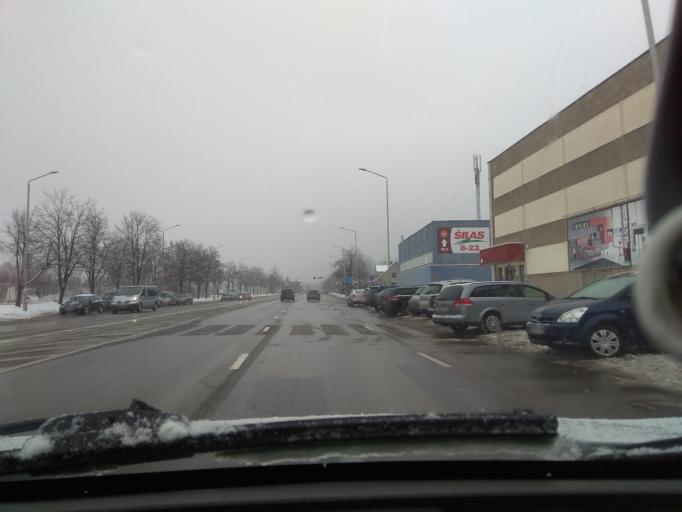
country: LT
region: Kauno apskritis
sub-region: Kaunas
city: Eiguliai
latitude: 54.9288
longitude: 23.9160
